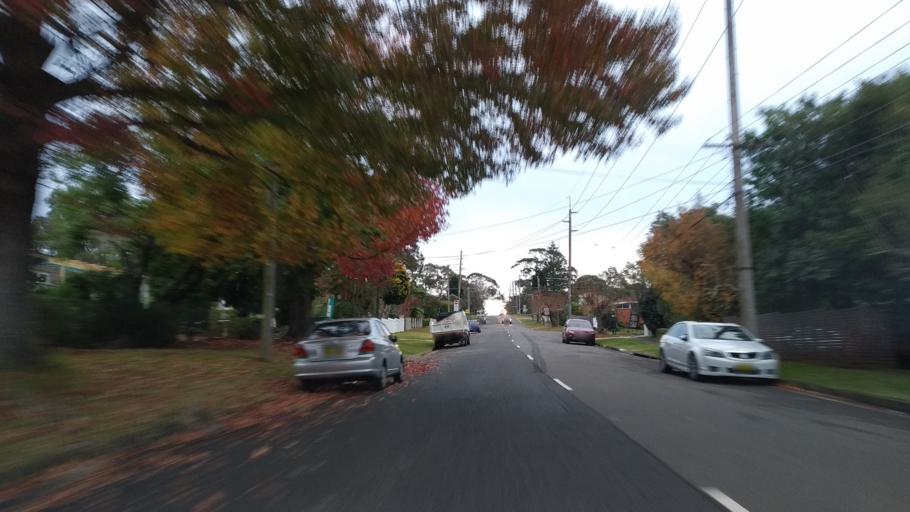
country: AU
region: New South Wales
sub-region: Warringah
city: Allambie Heights
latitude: -33.7491
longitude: 151.2456
